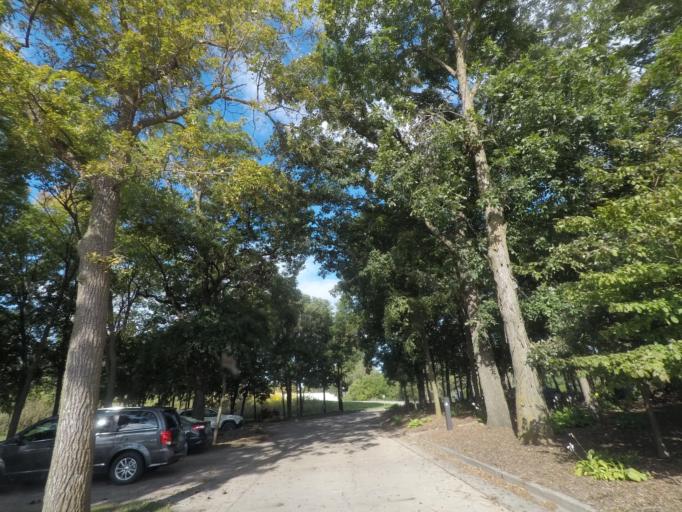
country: US
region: Iowa
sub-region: Story County
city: Nevada
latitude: 42.0070
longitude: -93.4436
